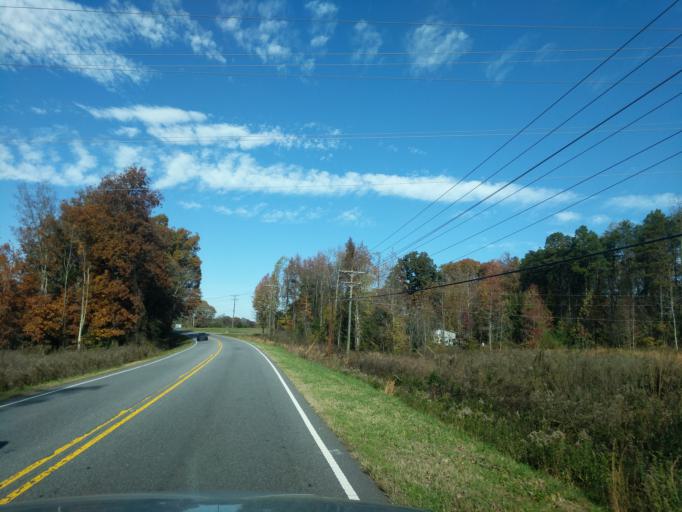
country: US
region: North Carolina
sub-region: Catawba County
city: Maiden
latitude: 35.6035
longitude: -81.2546
